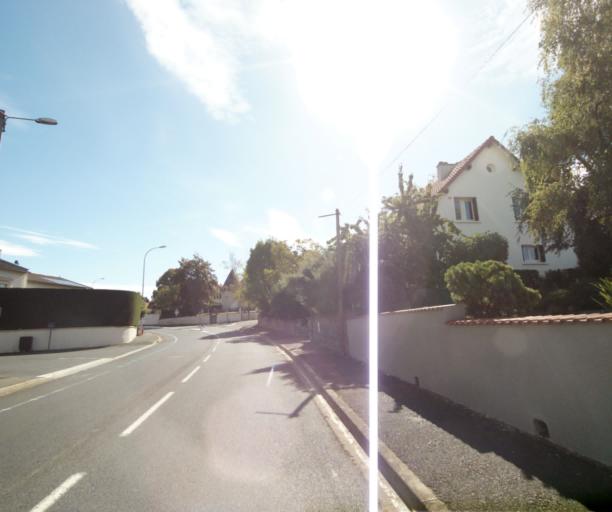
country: FR
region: Auvergne
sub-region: Departement du Puy-de-Dome
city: Cournon-d'Auvergne
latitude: 45.7663
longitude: 3.1998
